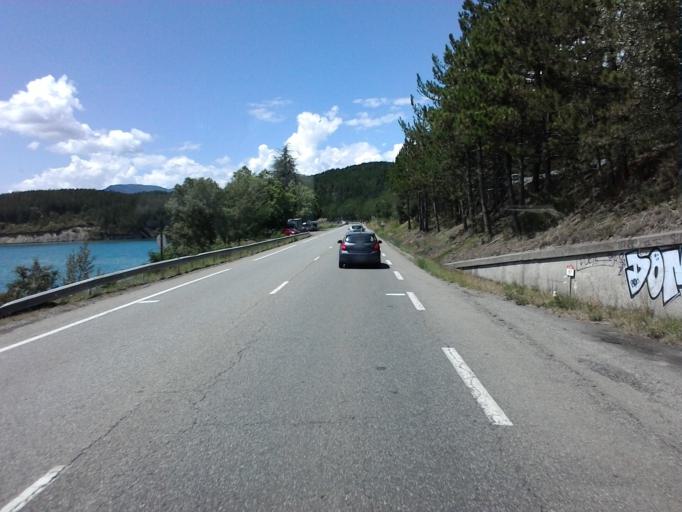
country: FR
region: Provence-Alpes-Cote d'Azur
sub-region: Departement des Hautes-Alpes
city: Chorges
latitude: 44.5356
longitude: 6.3841
